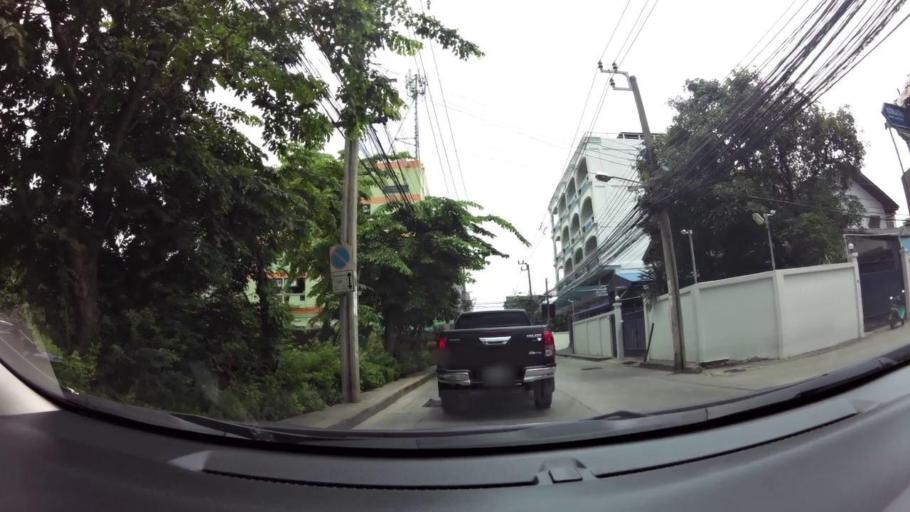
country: TH
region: Bangkok
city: Bang Na
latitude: 13.6816
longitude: 100.6365
